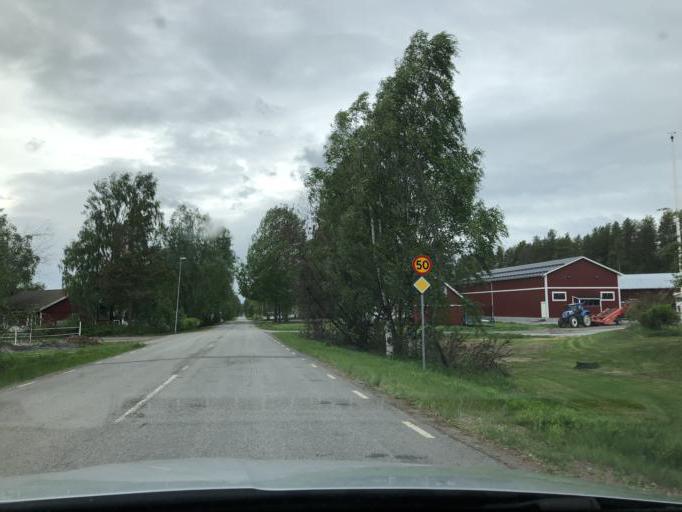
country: SE
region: Norrbotten
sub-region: Pitea Kommun
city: Bergsviken
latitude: 65.3854
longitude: 21.3269
